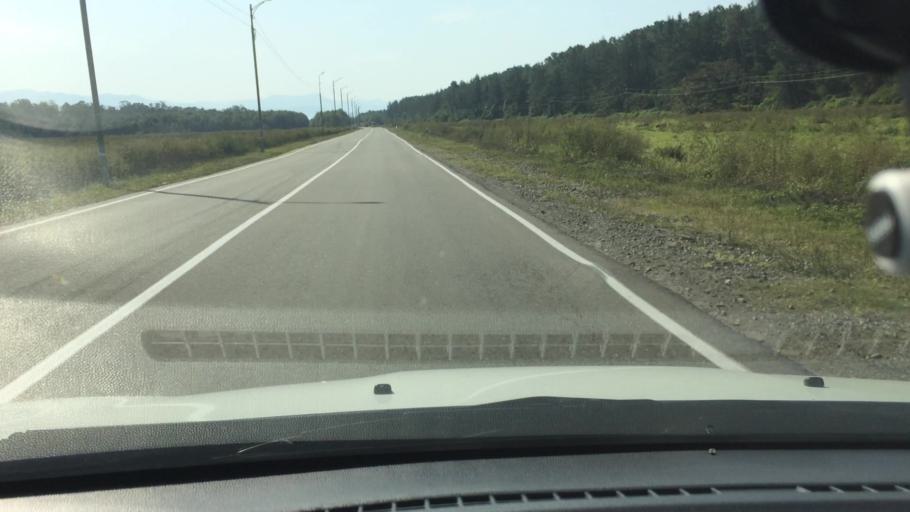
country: GE
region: Guria
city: Urek'i
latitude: 41.9518
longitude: 41.7704
